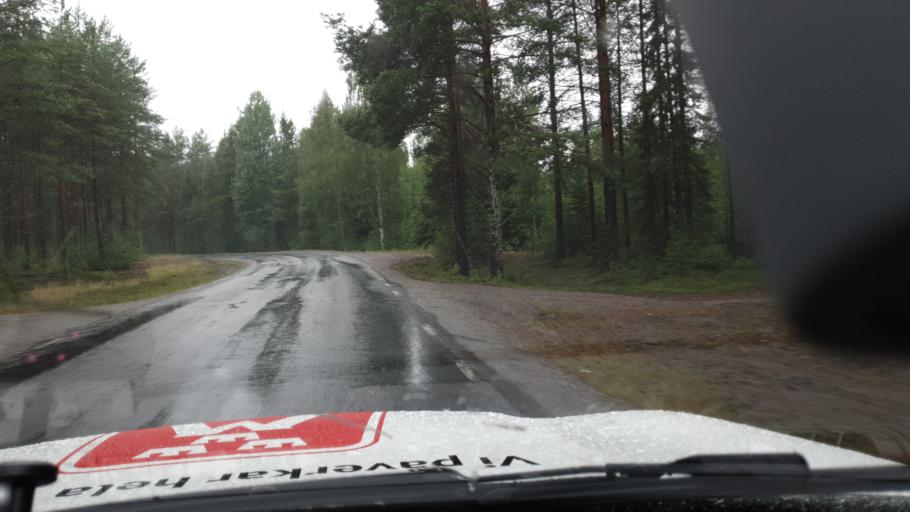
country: SE
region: Vaesterbotten
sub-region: Skelleftea Kommun
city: Burea
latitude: 64.6126
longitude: 21.1795
